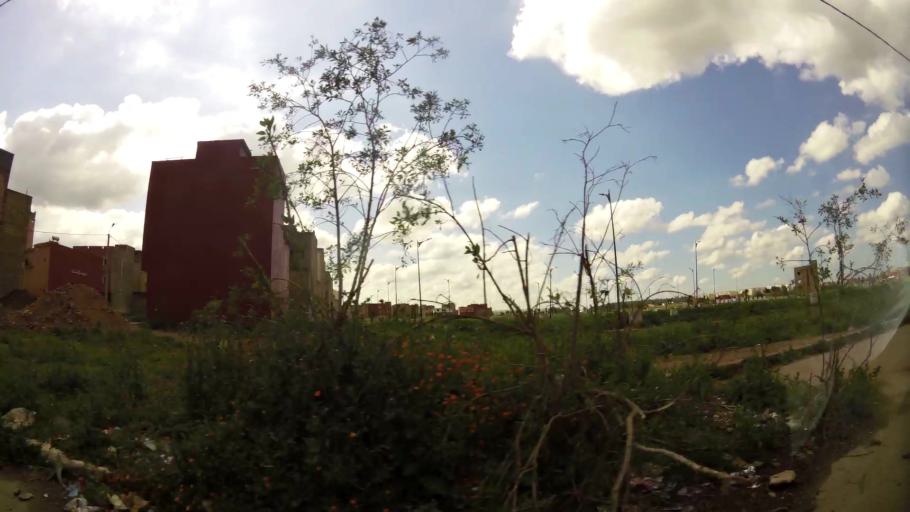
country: MA
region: Grand Casablanca
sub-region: Mediouna
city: Mediouna
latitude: 33.3638
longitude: -7.5336
